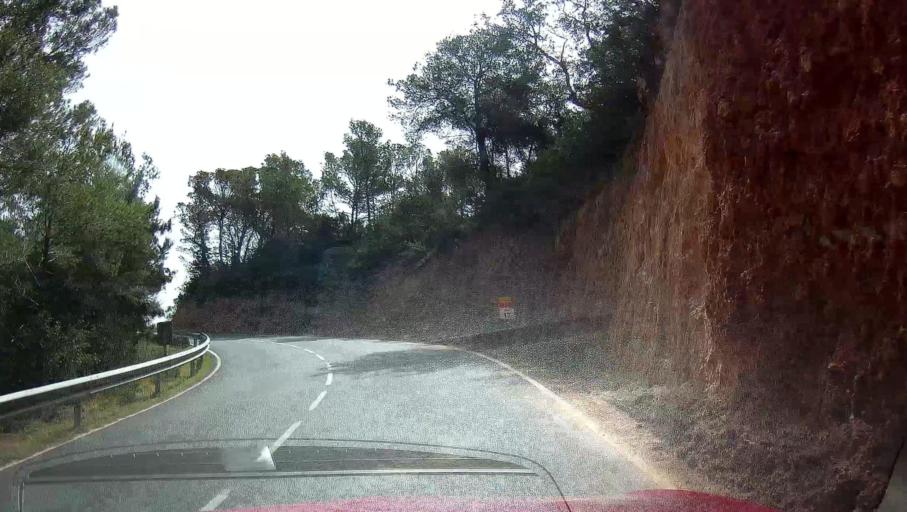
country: ES
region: Balearic Islands
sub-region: Illes Balears
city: Sant Joan de Labritja
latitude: 39.0623
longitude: 1.5834
